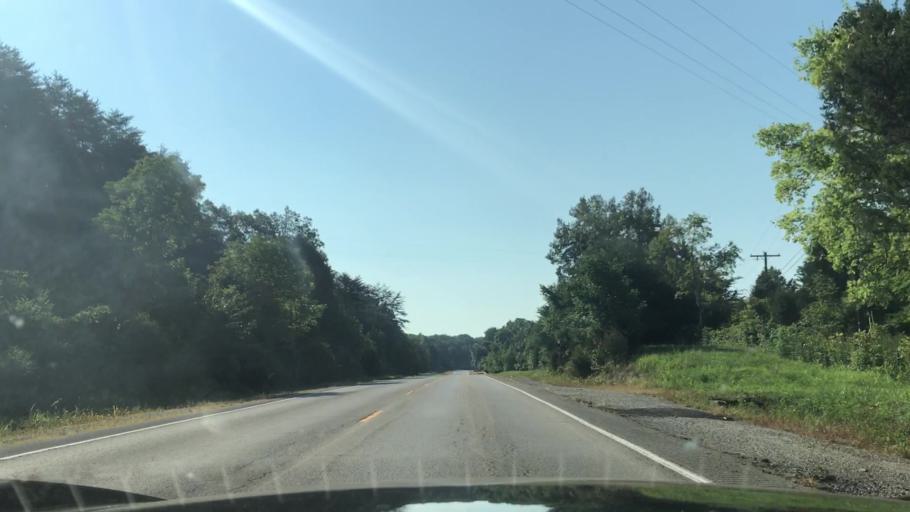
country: US
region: Kentucky
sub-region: Hart County
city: Horse Cave
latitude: 37.1975
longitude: -85.9310
